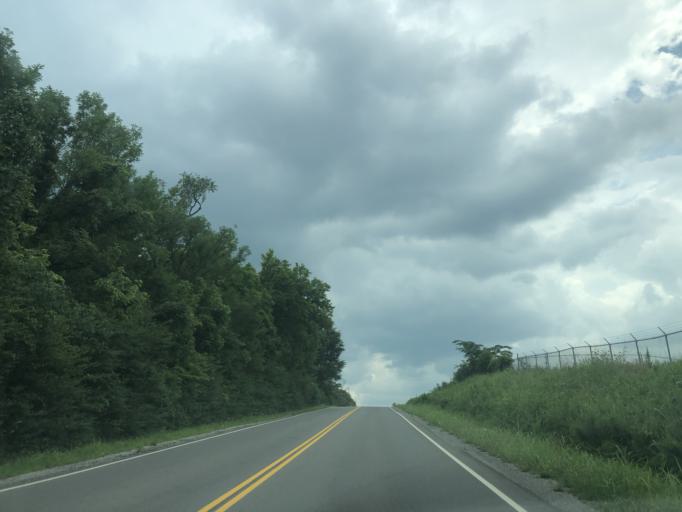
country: US
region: Tennessee
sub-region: Davidson County
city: Oak Hill
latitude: 36.1116
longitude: -86.6652
